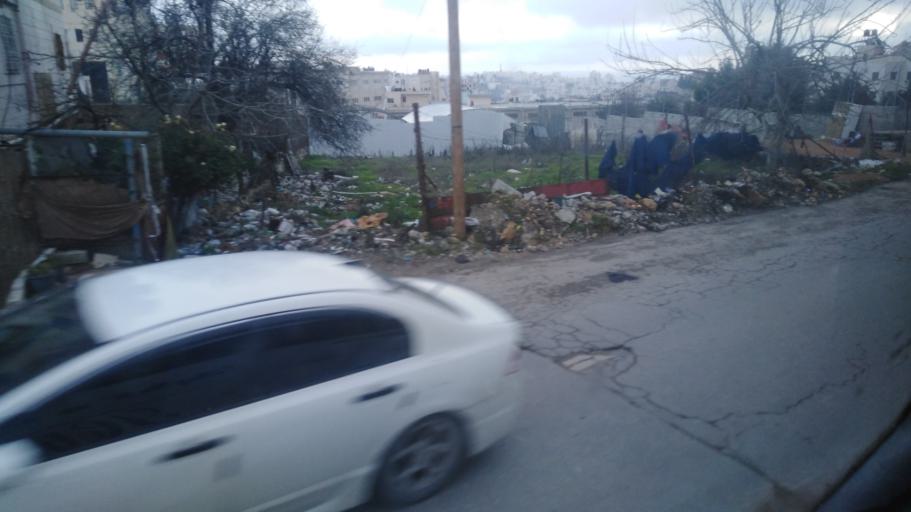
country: PS
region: West Bank
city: Hebron
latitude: 31.5283
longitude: 35.0788
